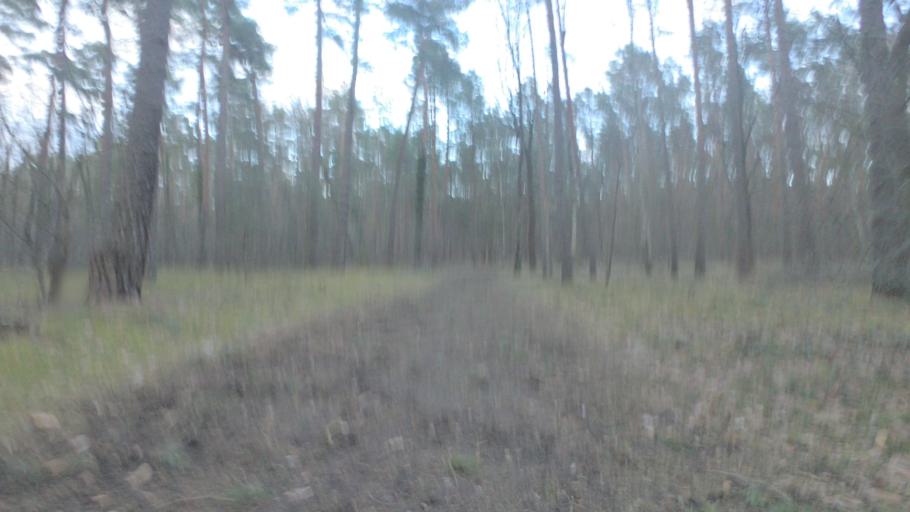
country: DE
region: Brandenburg
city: Rangsdorf
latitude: 52.2657
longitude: 13.3557
